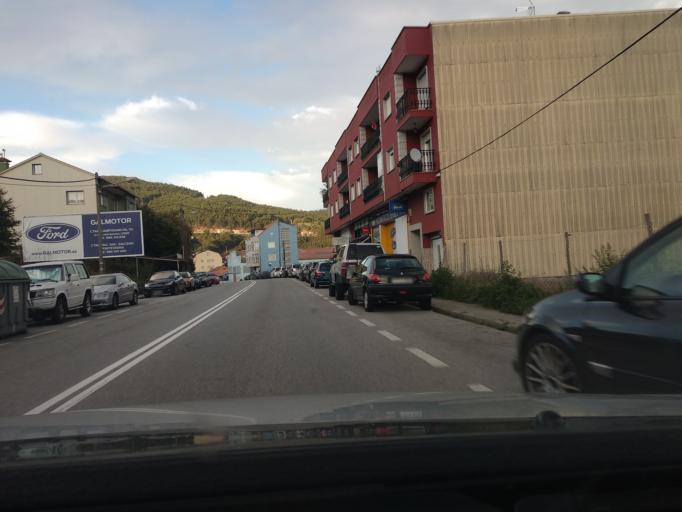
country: ES
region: Galicia
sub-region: Provincia de Pontevedra
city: Vigo
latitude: 42.2869
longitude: -8.6818
